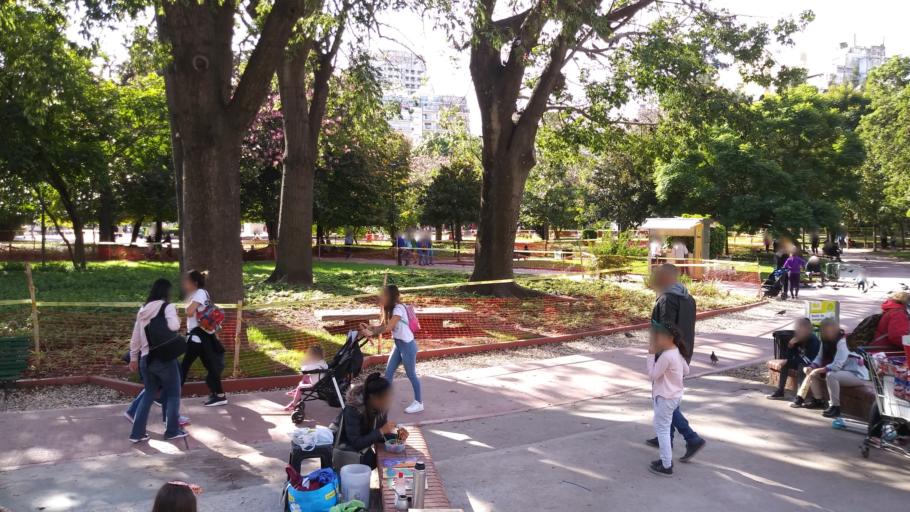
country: AR
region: Buenos Aires F.D.
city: Colegiales
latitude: -34.6187
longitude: -58.4325
